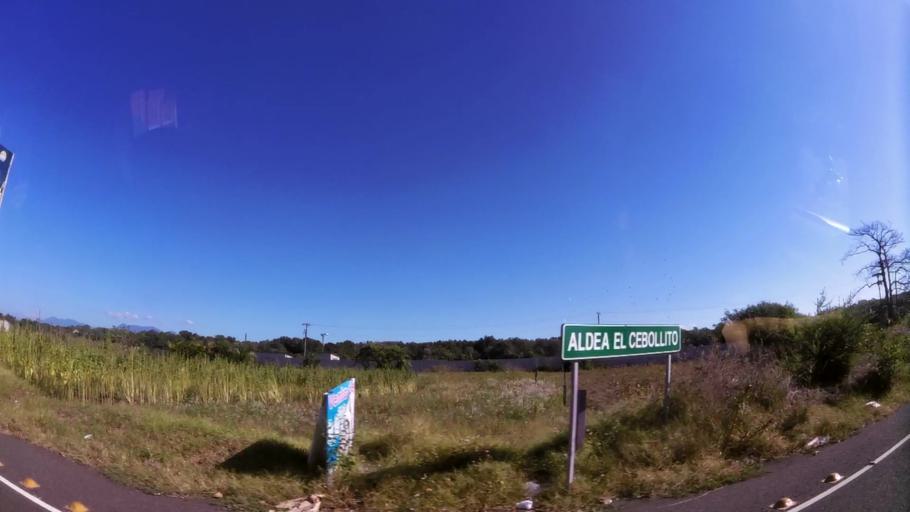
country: GT
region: Santa Rosa
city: Guazacapan
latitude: 13.8680
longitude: -90.4137
